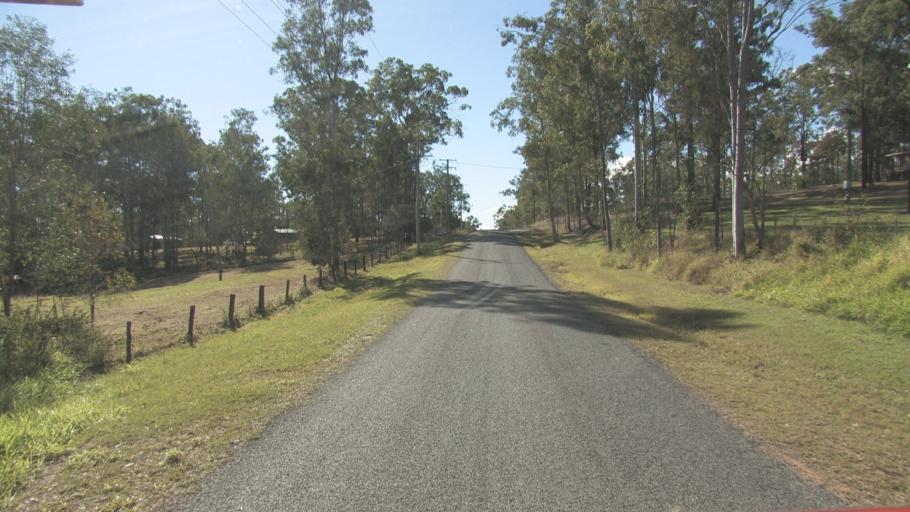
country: AU
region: Queensland
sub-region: Logan
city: Chambers Flat
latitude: -27.8109
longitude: 153.0784
